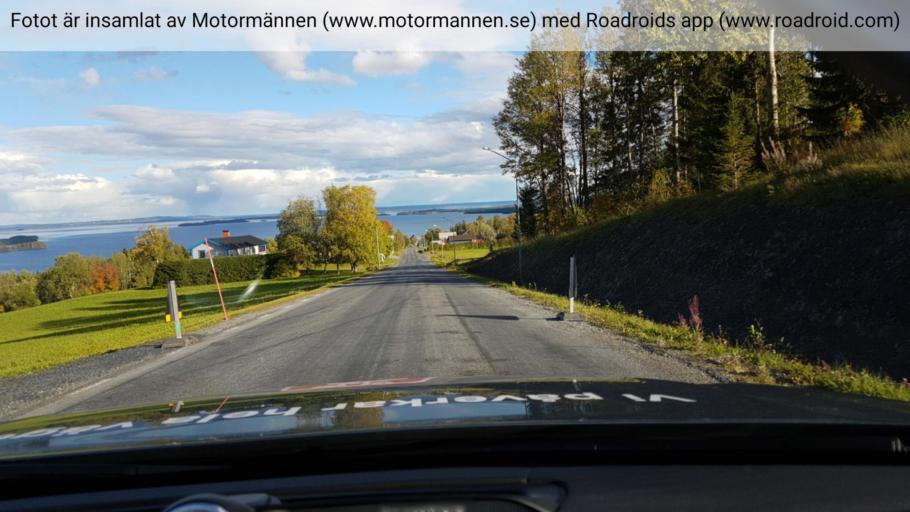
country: SE
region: Jaemtland
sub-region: Krokoms Kommun
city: Krokom
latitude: 63.1820
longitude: 14.0663
